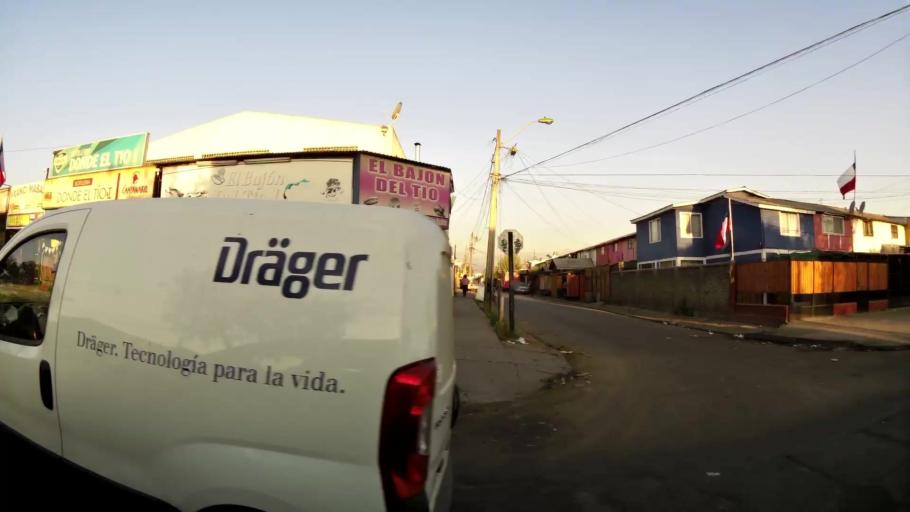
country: CL
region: Santiago Metropolitan
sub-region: Provincia de Maipo
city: San Bernardo
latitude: -33.5809
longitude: -70.6761
